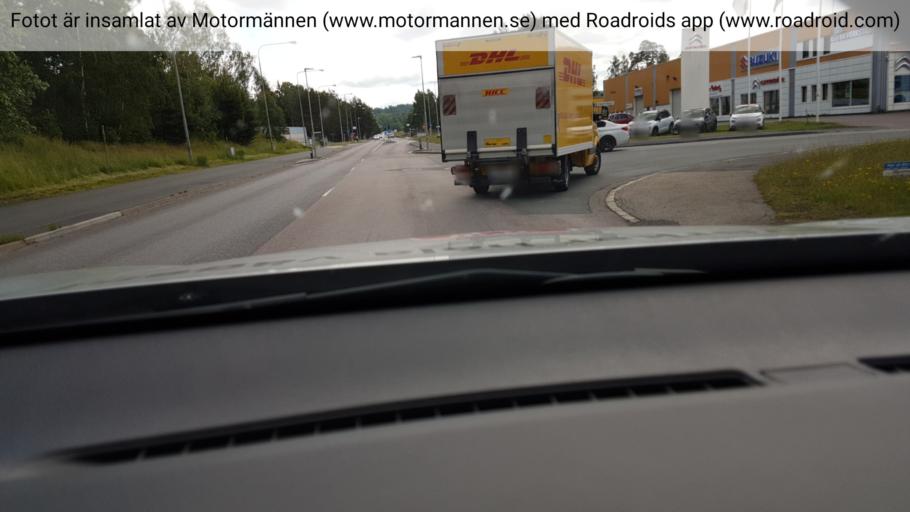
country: SE
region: Joenkoeping
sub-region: Jonkopings Kommun
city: Jonkoping
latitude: 57.7550
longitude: 14.1702
